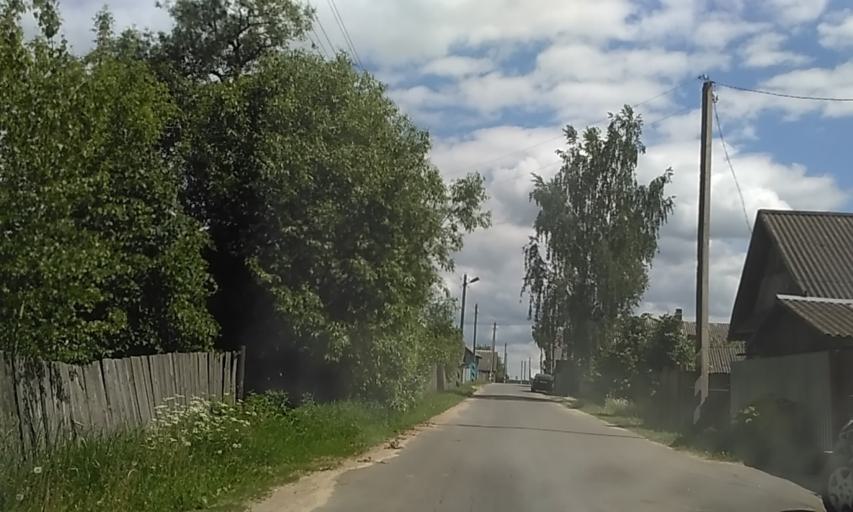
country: BY
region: Minsk
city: Krupki
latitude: 54.3489
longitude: 29.1313
